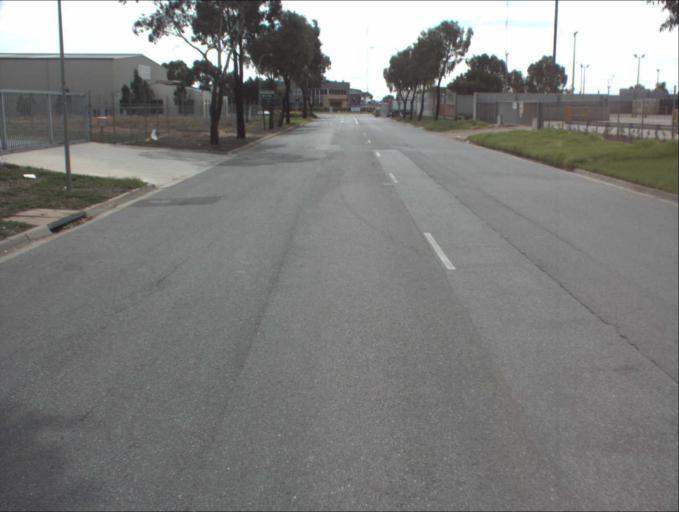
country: AU
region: South Australia
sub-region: Port Adelaide Enfield
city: Blair Athol
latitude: -34.8420
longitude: 138.5700
